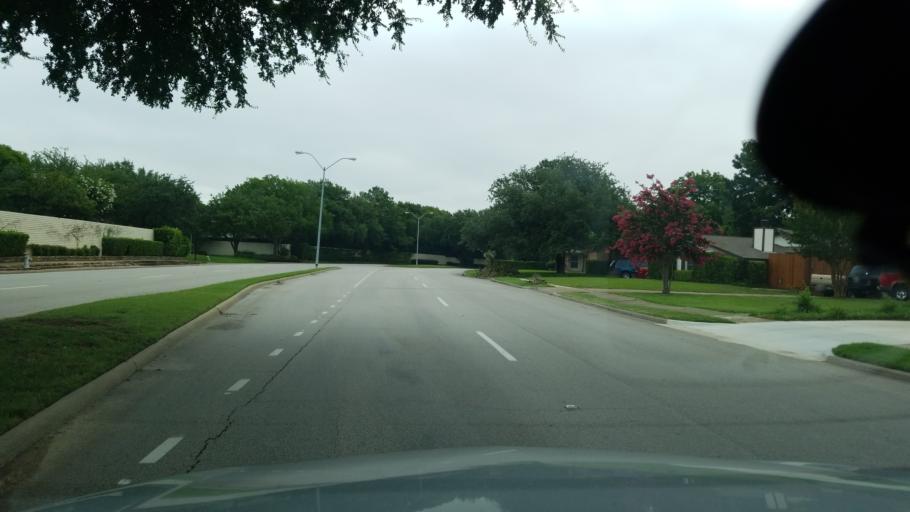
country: US
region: Texas
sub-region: Dallas County
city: Irving
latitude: 32.8538
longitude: -96.9489
